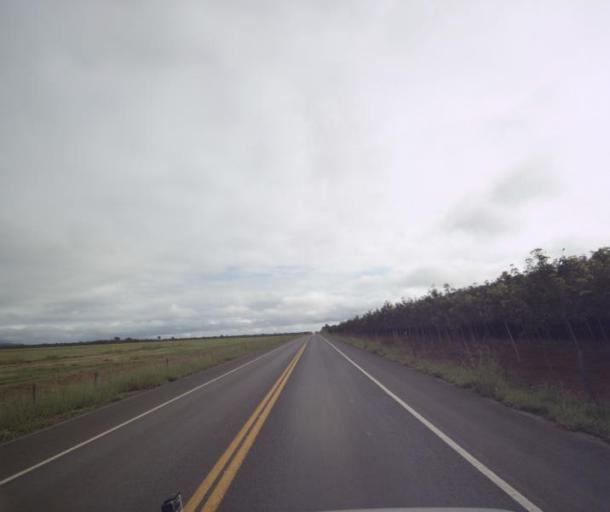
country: BR
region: Goias
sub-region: Padre Bernardo
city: Padre Bernardo
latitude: -15.3772
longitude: -48.6453
